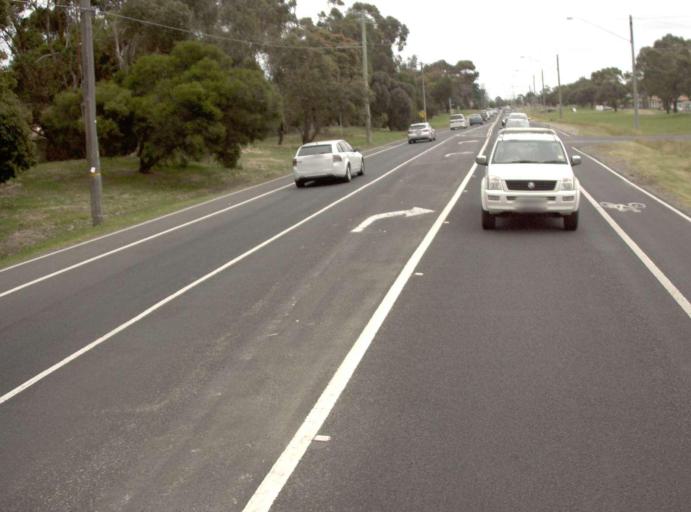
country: AU
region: Victoria
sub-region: Mornington Peninsula
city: Mount Martha
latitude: -38.2536
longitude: 145.0362
